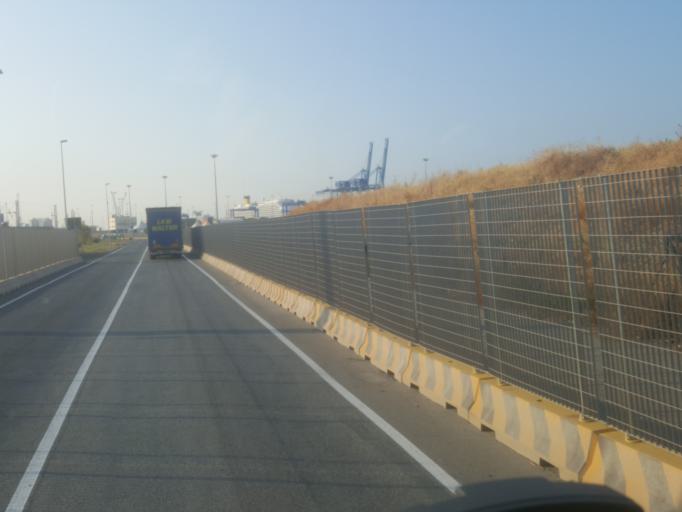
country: IT
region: Latium
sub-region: Citta metropolitana di Roma Capitale
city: Aurelia
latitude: 42.1128
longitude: 11.7707
